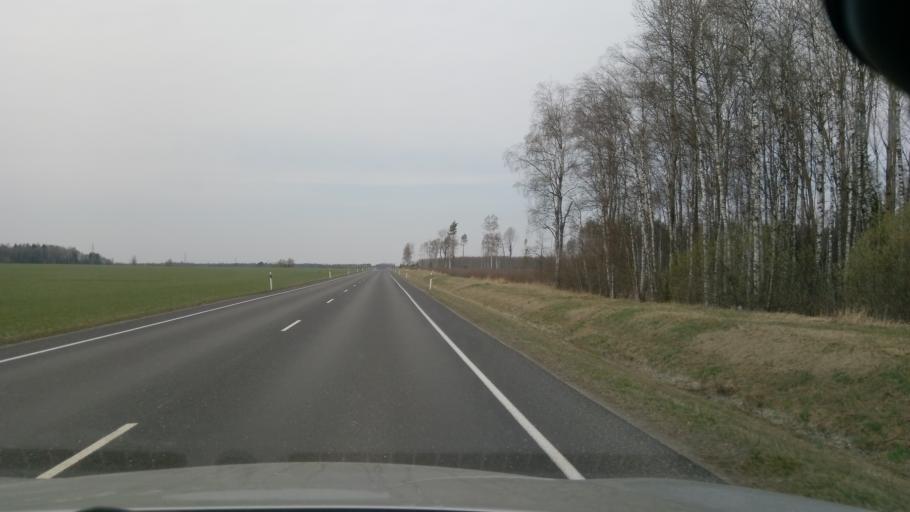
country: EE
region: Viljandimaa
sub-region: Vohma linn
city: Vohma
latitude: 58.7214
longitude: 25.6051
